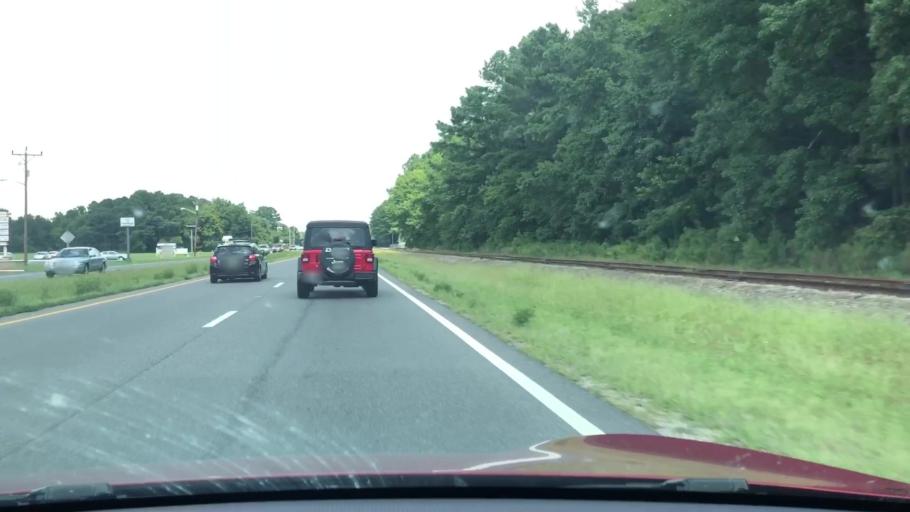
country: US
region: Virginia
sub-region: Northampton County
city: Exmore
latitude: 37.5444
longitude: -75.8124
